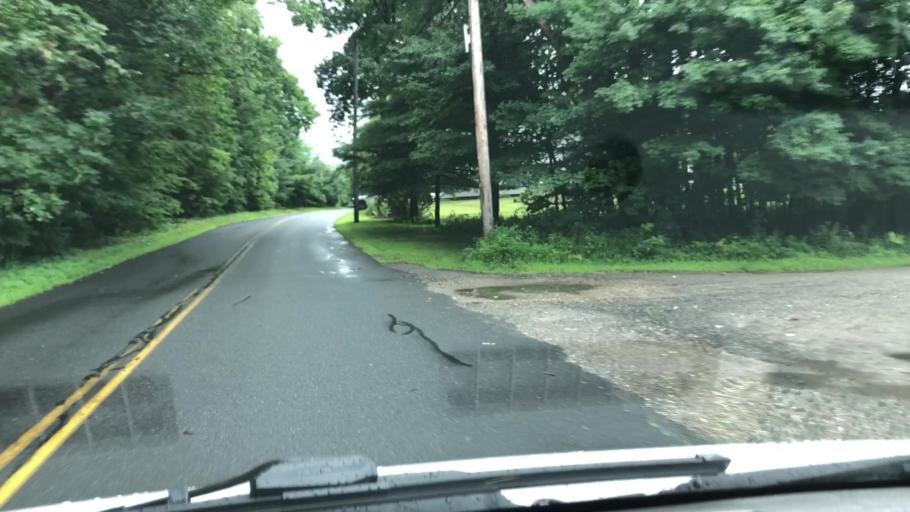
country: US
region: Massachusetts
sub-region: Hampshire County
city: Williamsburg
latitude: 42.3575
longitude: -72.7015
